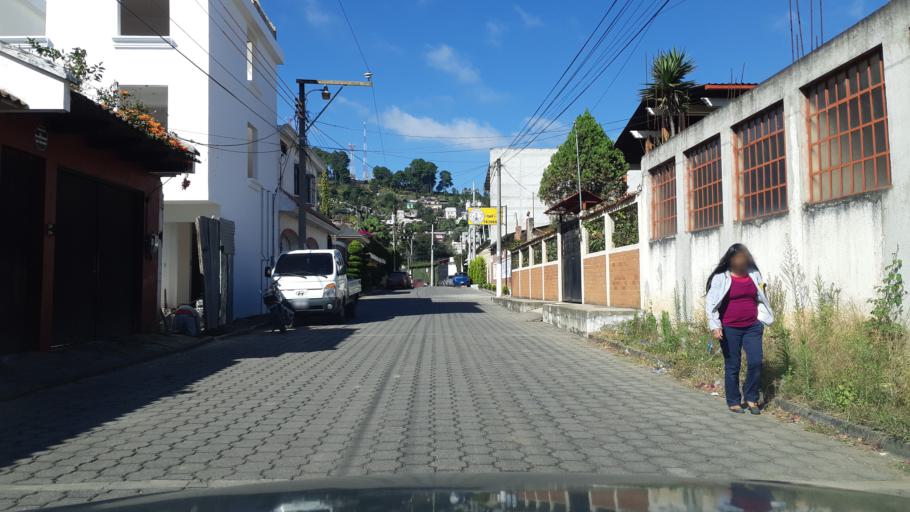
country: GT
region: Chimaltenango
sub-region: Municipio de Chimaltenango
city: Chimaltenango
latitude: 14.6517
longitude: -90.8171
